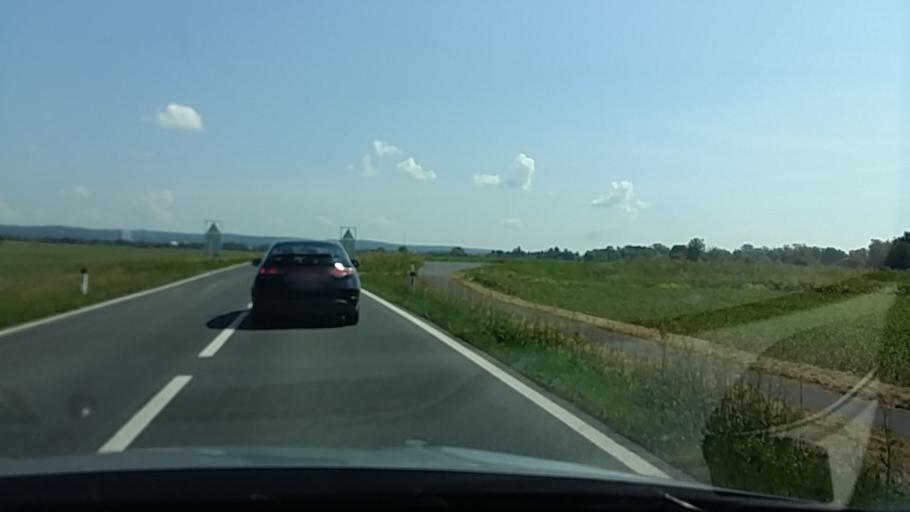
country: AT
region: Burgenland
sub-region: Politischer Bezirk Jennersdorf
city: Mogersdorf
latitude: 46.9500
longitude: 16.2412
